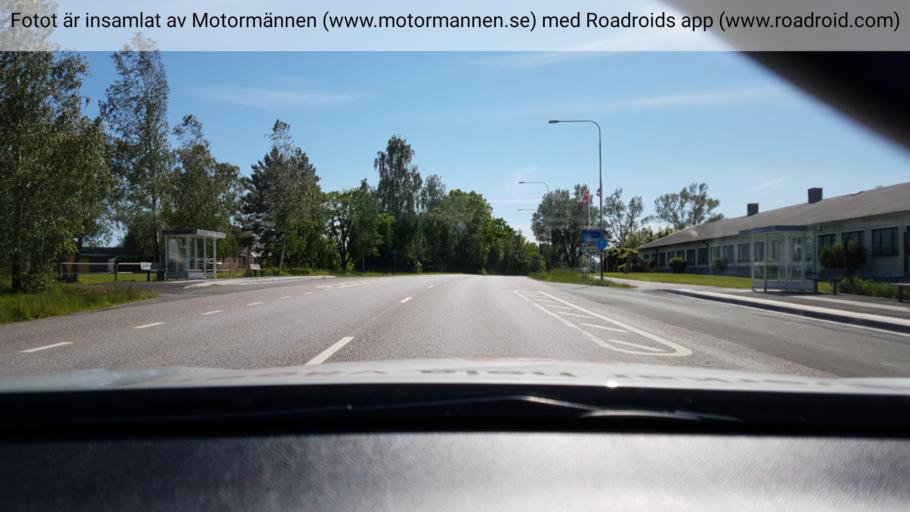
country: SE
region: Vaestra Goetaland
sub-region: Tibro Kommun
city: Tibro
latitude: 58.4255
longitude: 14.1406
